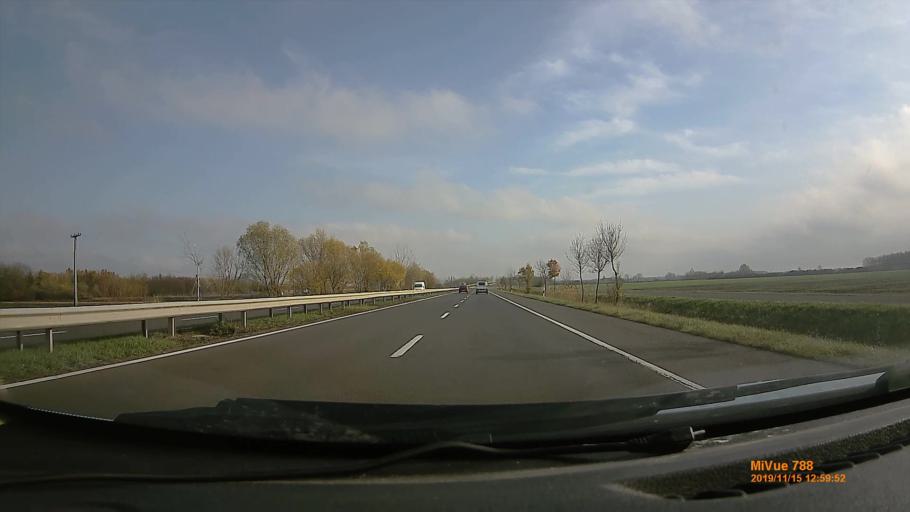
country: HU
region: Bekes
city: Doboz
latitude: 46.6642
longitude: 21.1979
